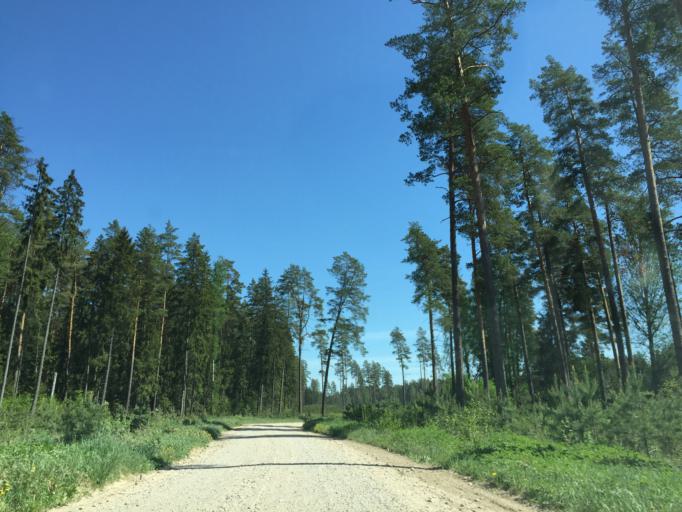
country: LV
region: Ogre
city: Ogre
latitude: 56.7445
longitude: 24.5619
